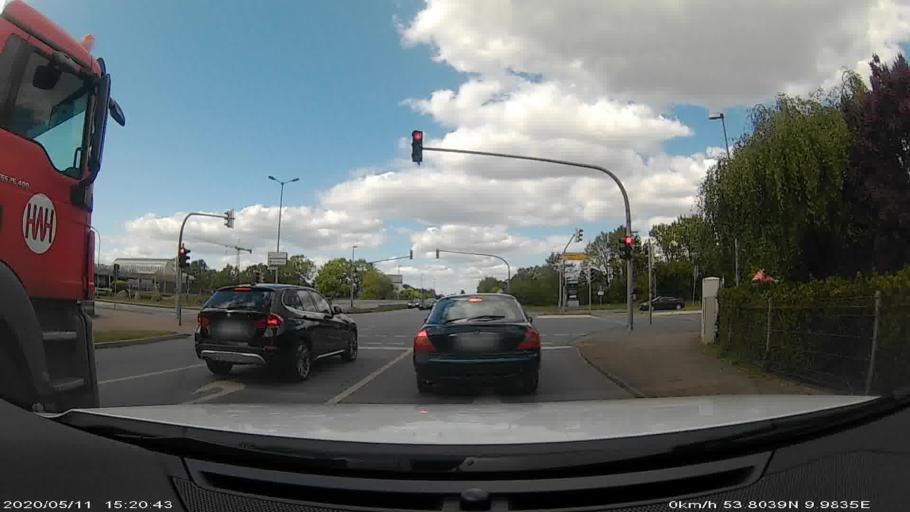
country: DE
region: Schleswig-Holstein
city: Kisdorf
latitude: 53.8055
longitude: 10.0001
